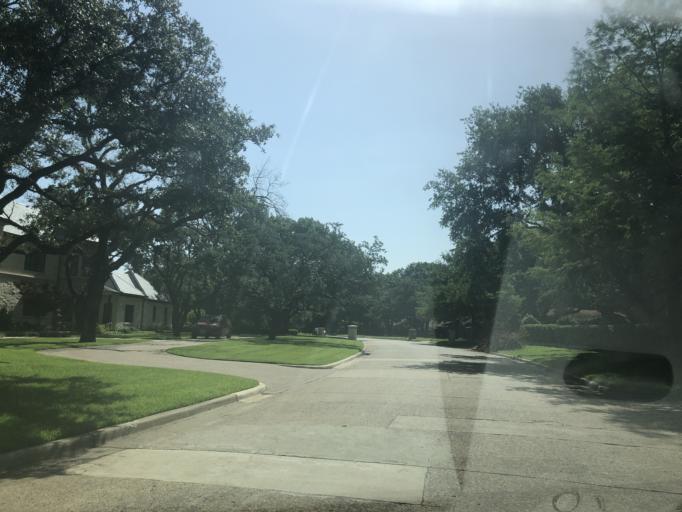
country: US
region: Texas
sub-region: Dallas County
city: University Park
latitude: 32.8851
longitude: -96.8173
